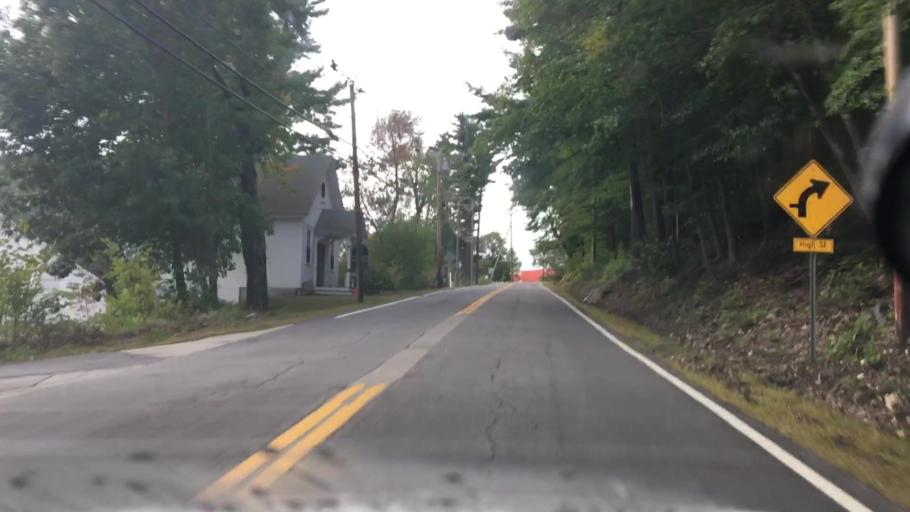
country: US
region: New Hampshire
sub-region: Carroll County
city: Sanbornville
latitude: 43.5570
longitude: -71.0285
